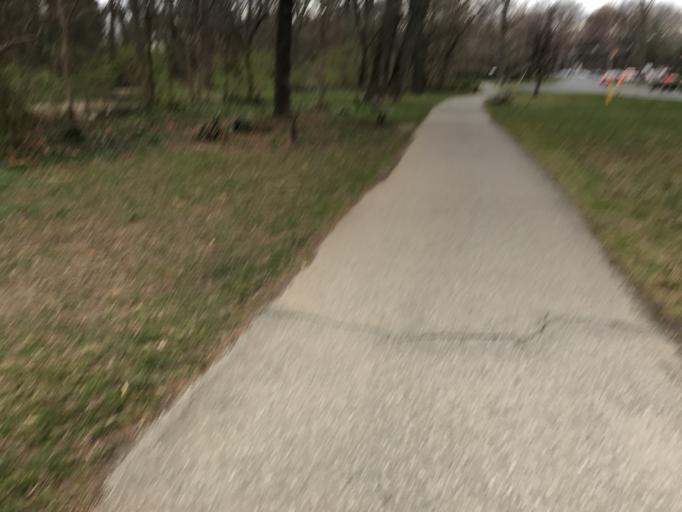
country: US
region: Maryland
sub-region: Montgomery County
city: Four Corners
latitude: 39.0070
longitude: -77.0184
